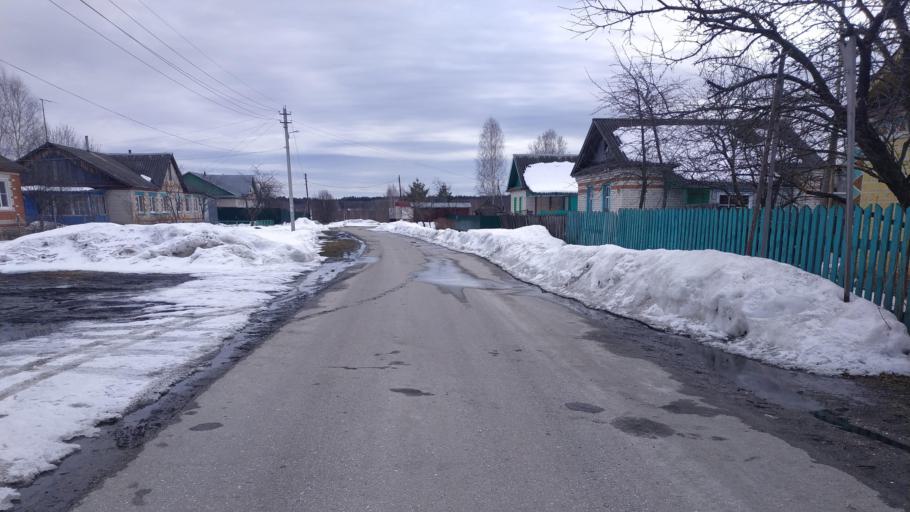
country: RU
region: Nizjnij Novgorod
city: Semenov
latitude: 56.7767
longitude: 44.2877
